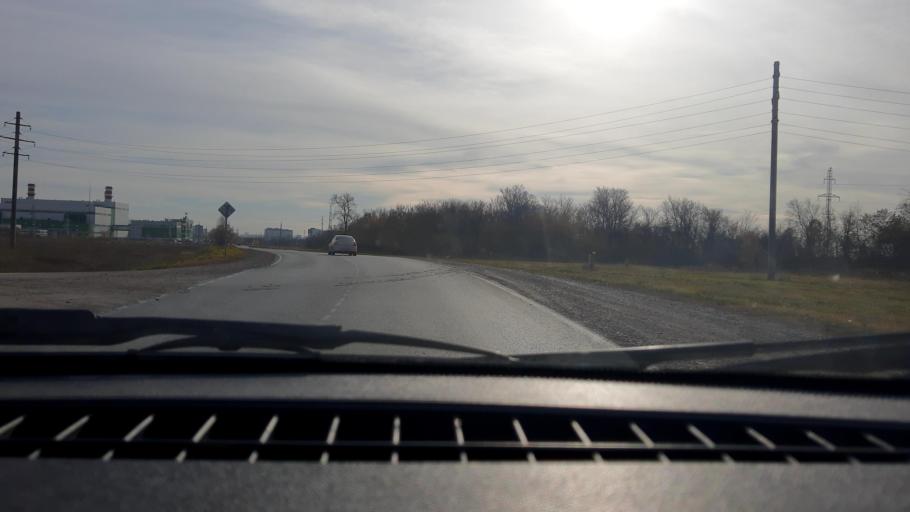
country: RU
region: Bashkortostan
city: Mikhaylovka
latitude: 54.8049
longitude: 55.8242
